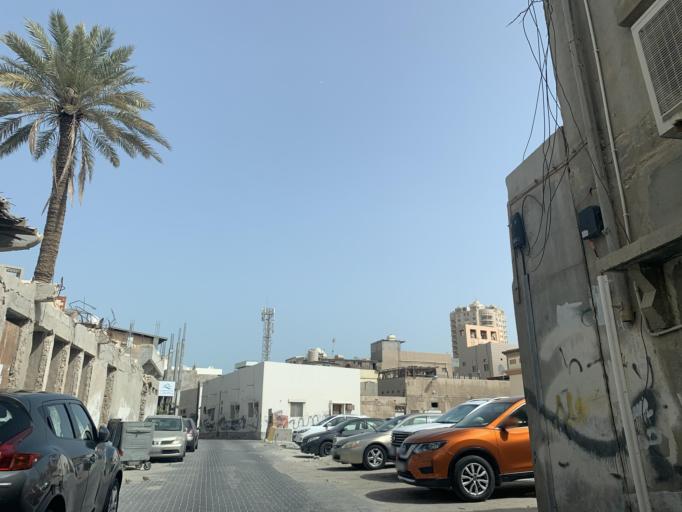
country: BH
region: Manama
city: Manama
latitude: 26.2276
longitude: 50.5685
